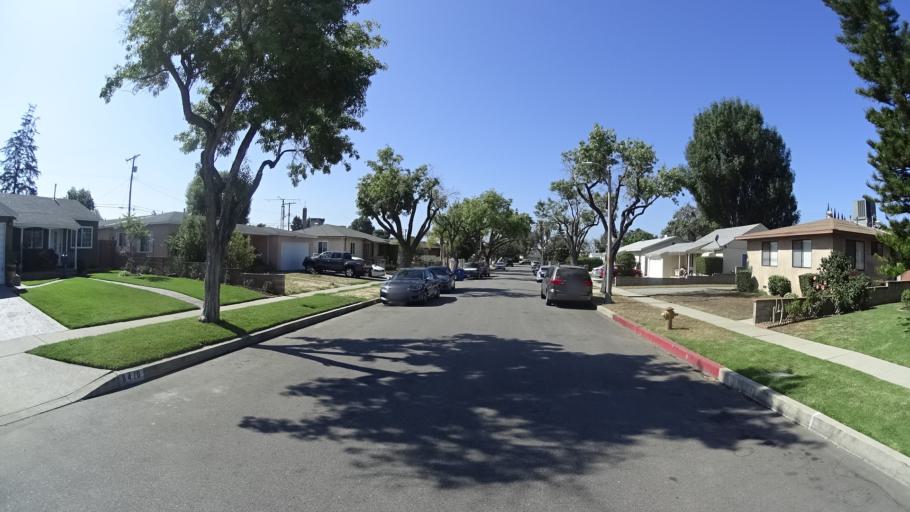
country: US
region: California
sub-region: Los Angeles County
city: Van Nuys
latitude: 34.2240
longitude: -118.4418
